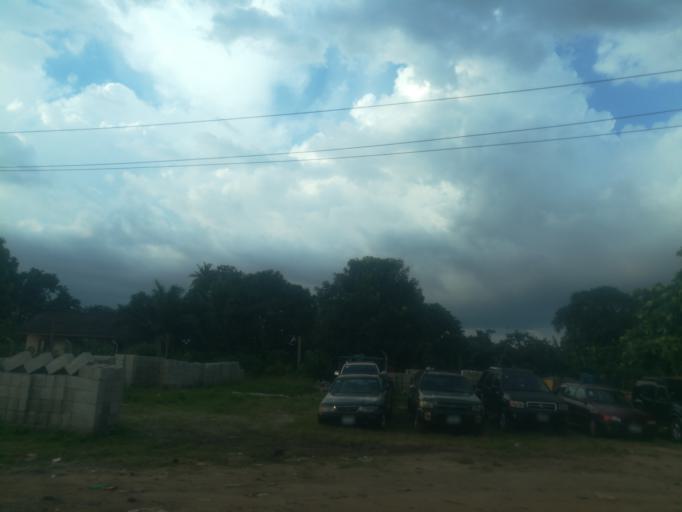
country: NG
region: Oyo
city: Ibadan
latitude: 7.3791
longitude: 3.8453
